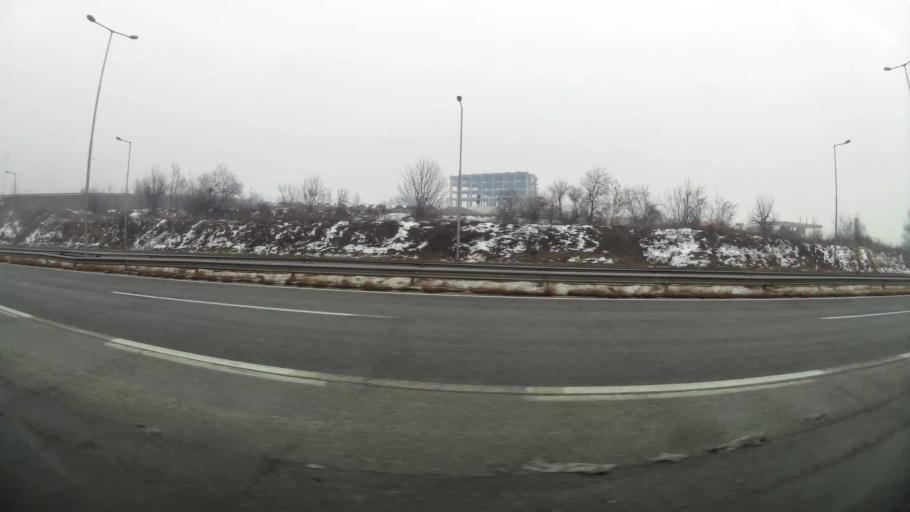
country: MK
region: Petrovec
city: Petrovec
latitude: 41.9581
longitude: 21.6316
